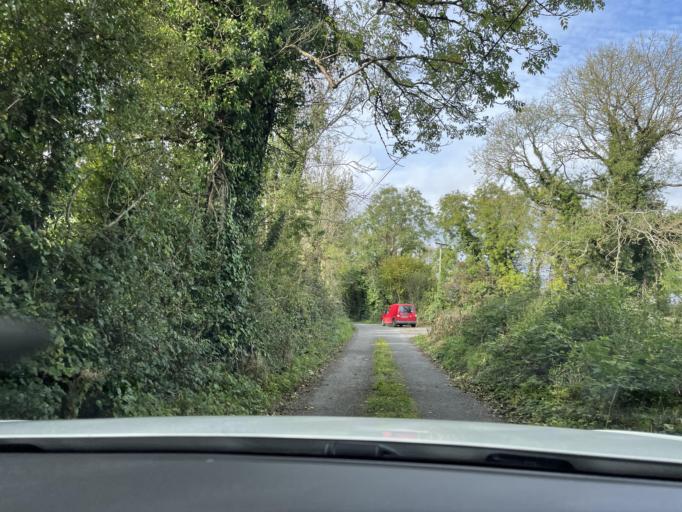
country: IE
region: Connaught
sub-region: County Leitrim
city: Carrick-on-Shannon
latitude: 53.9623
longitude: -8.0720
